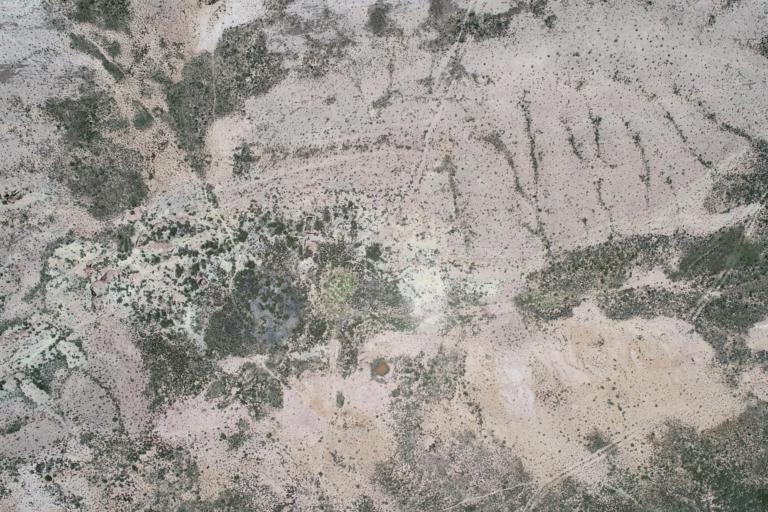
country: BO
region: La Paz
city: Patacamaya
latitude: -17.2818
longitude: -68.4994
